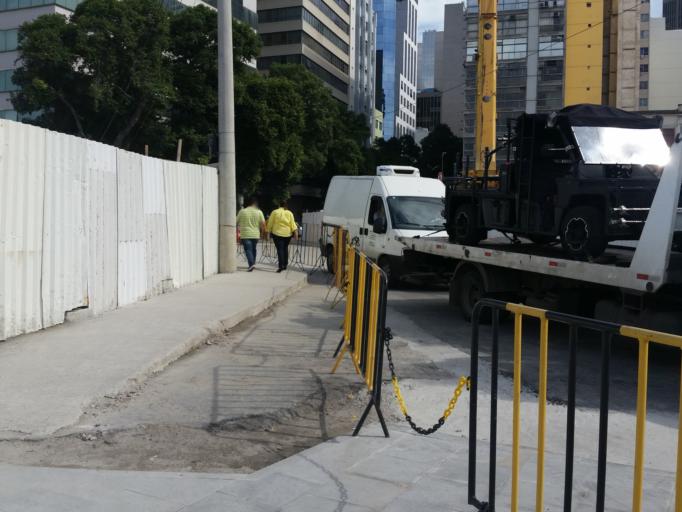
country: BR
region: Rio de Janeiro
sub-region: Rio De Janeiro
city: Rio de Janeiro
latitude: -22.8987
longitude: -43.1765
